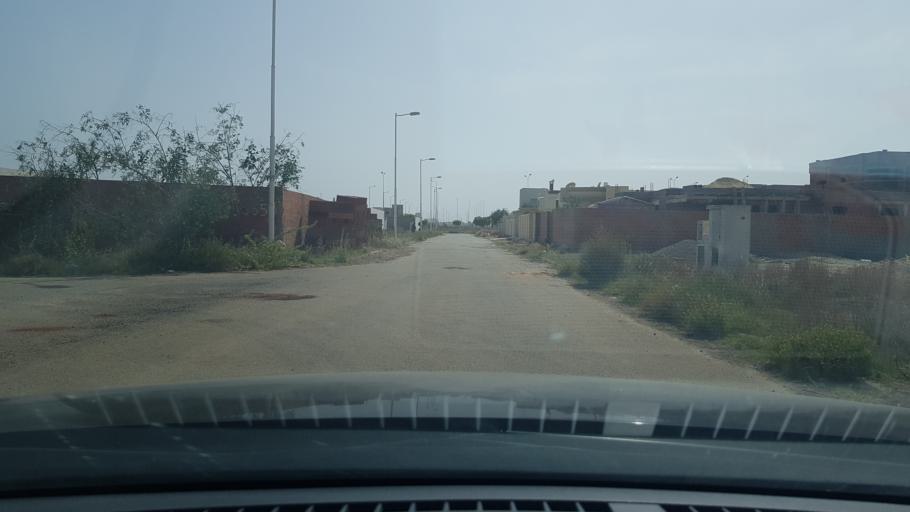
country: TN
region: Safaqis
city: Al Qarmadah
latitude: 34.8385
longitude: 10.7610
